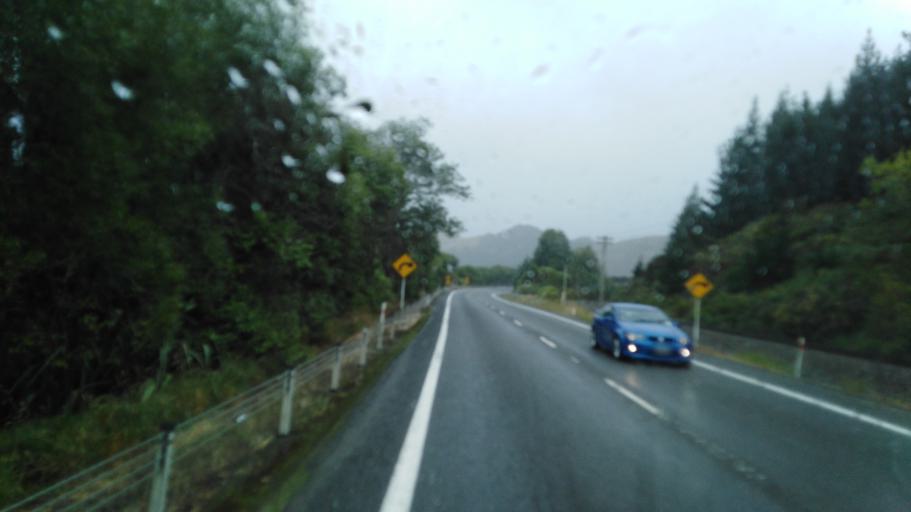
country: NZ
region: Marlborough
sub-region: Marlborough District
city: Blenheim
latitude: -41.4244
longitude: 173.9594
